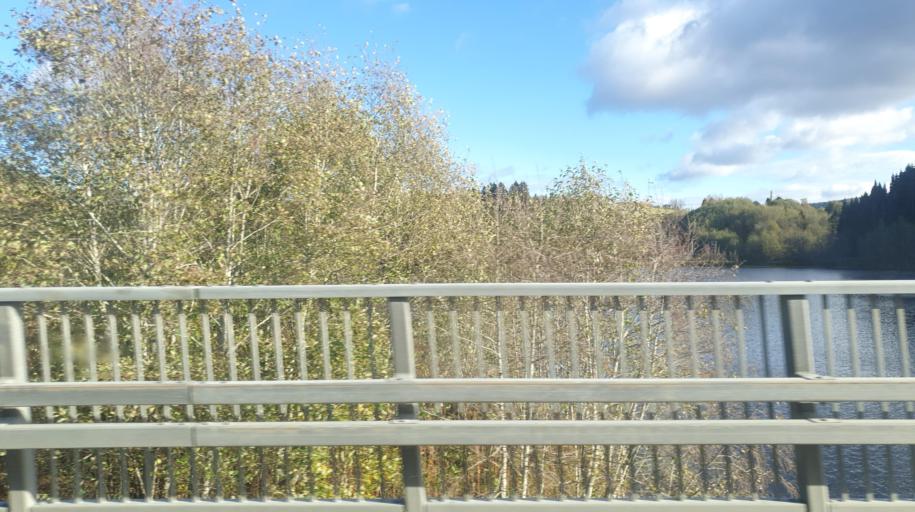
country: NO
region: Sor-Trondelag
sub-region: Klaebu
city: Klaebu
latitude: 63.3111
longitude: 10.4516
